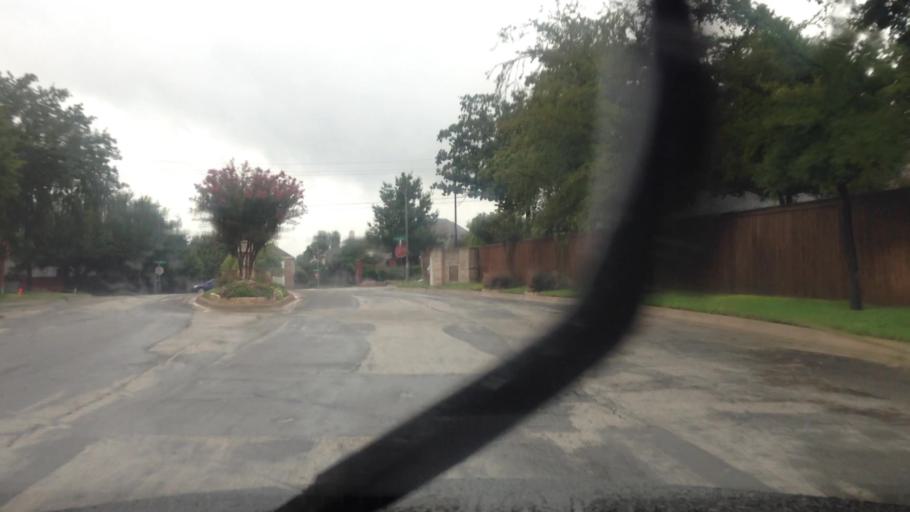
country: US
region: Texas
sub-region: Tarrant County
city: Keller
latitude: 32.9076
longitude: -97.2324
